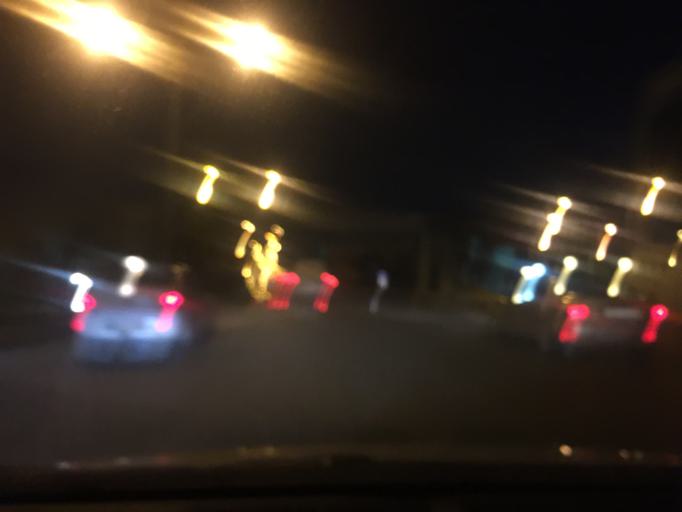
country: JO
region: Amman
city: Amman
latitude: 31.9895
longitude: 35.9178
